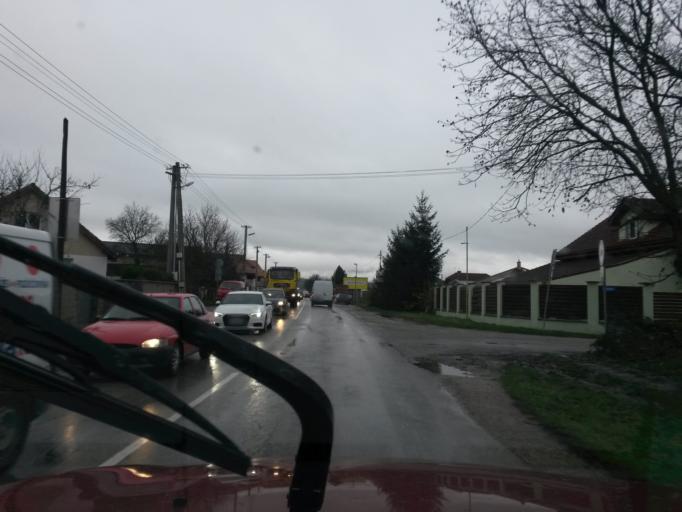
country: SK
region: Kosicky
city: Kosice
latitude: 48.6666
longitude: 21.3267
